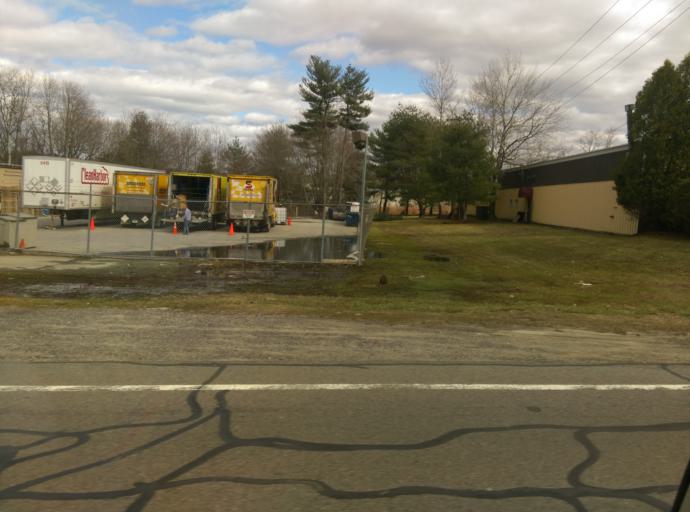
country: US
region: Massachusetts
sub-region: Essex County
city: Salisbury
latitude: 42.8592
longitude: -70.8916
